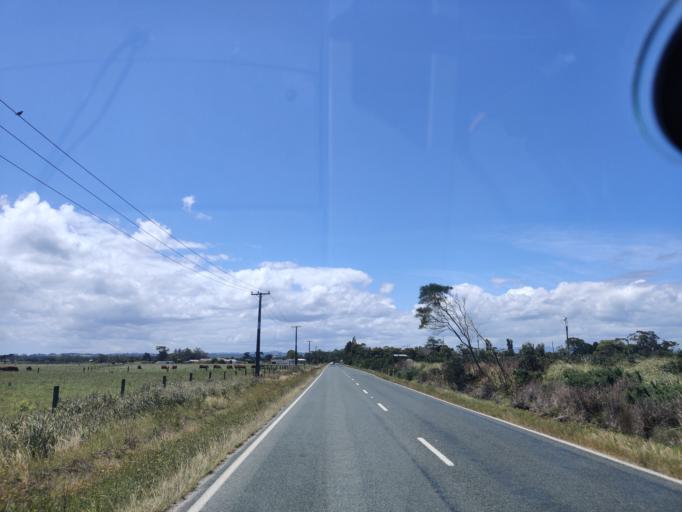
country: NZ
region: Northland
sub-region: Far North District
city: Kaitaia
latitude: -35.0231
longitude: 173.2227
